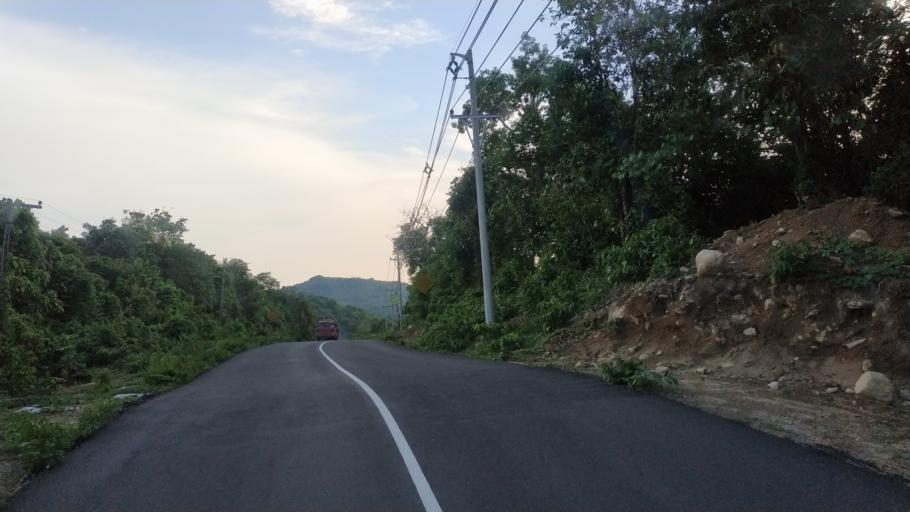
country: MM
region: Mon
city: Kyaikto
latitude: 17.4347
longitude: 97.0951
